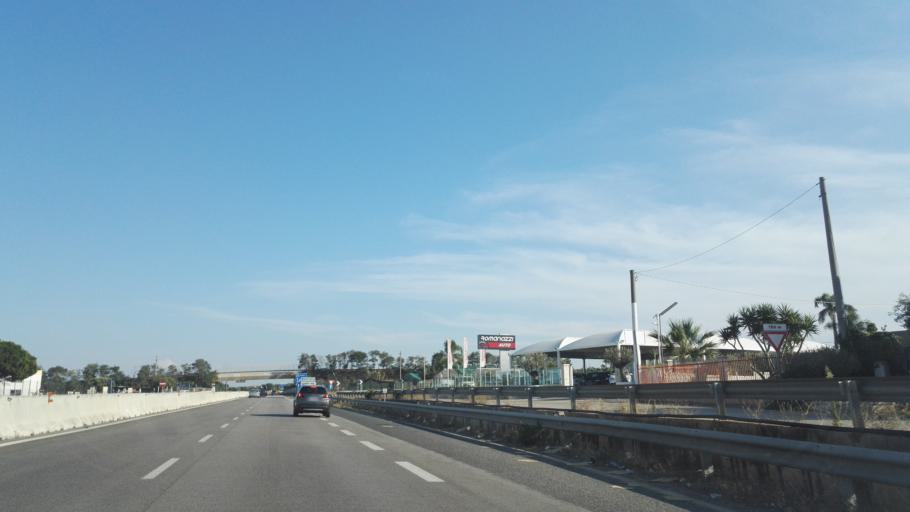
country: IT
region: Apulia
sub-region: Provincia di Bari
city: Polignano a Mare
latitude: 40.9932
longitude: 17.2058
